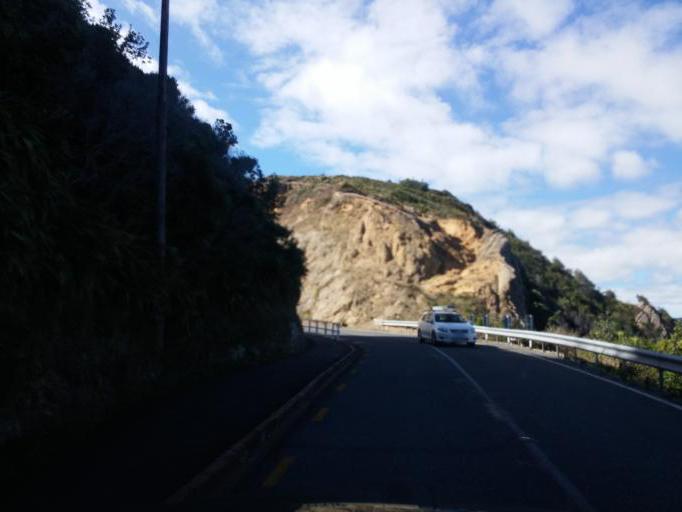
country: NZ
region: Wellington
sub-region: Wellington City
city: Wellington
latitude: -41.3297
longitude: 174.8318
